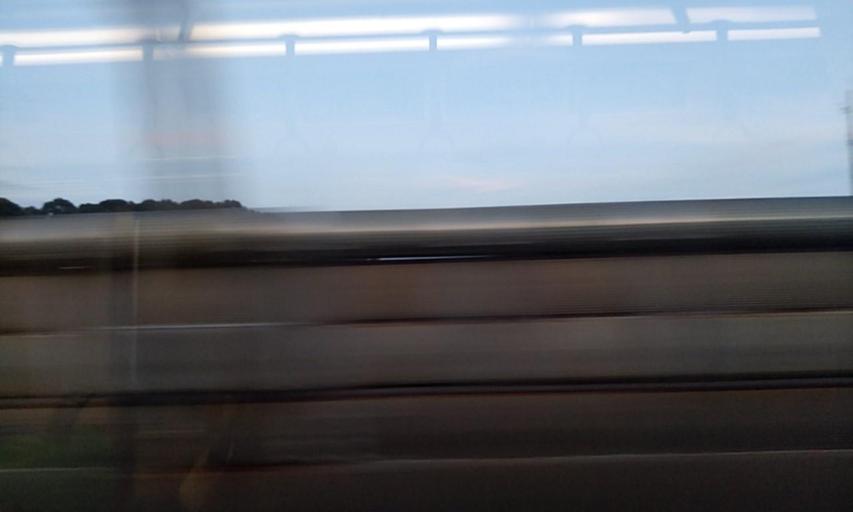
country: JP
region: Okayama
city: Kurashiki
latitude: 34.4698
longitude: 133.8096
